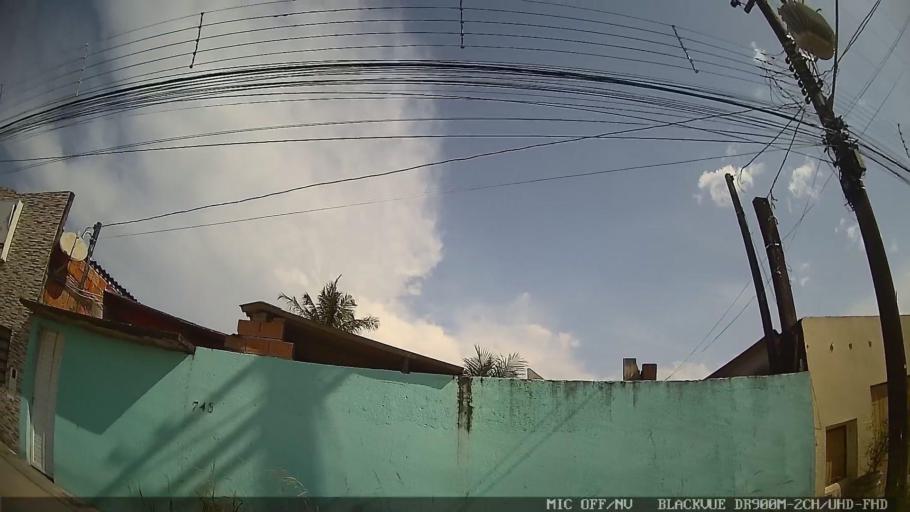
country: BR
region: Sao Paulo
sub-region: Guaruja
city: Guaruja
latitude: -23.9770
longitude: -46.2021
